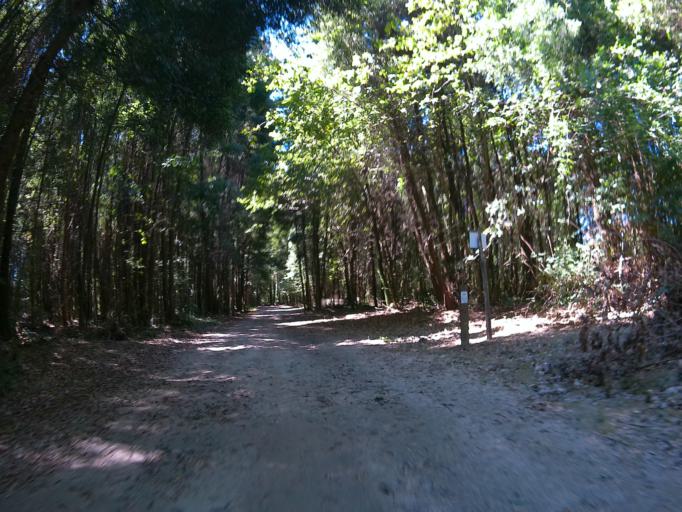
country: PT
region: Viana do Castelo
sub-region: Viana do Castelo
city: Darque
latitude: 41.7099
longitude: -8.7214
